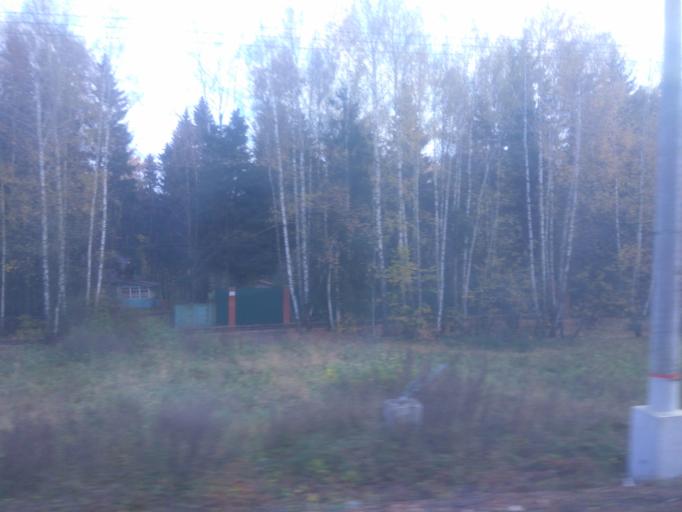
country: RU
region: Moscow
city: Tolstopal'tsevo
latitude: 55.6129
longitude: 37.1970
